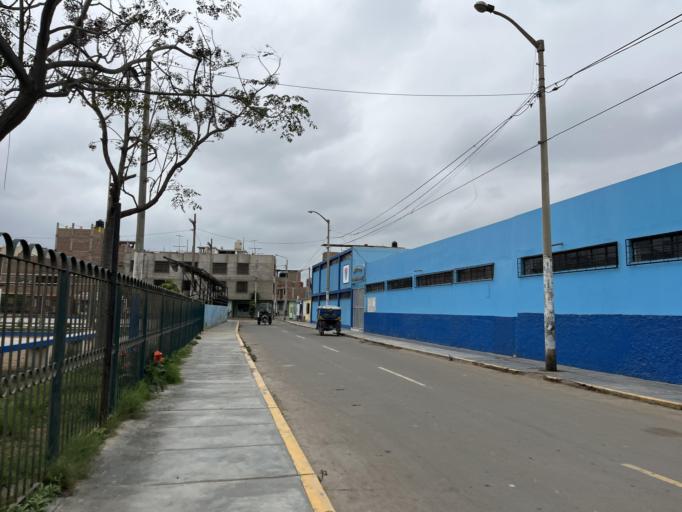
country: PE
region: La Libertad
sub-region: Provincia de Trujillo
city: Trujillo
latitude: -8.1144
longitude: -79.0055
